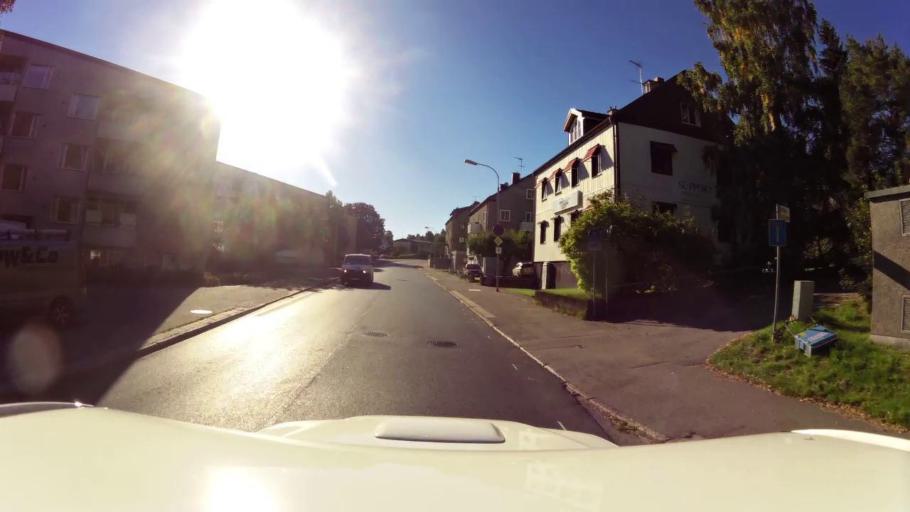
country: SE
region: OEstergoetland
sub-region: Linkopings Kommun
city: Linkoping
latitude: 58.3971
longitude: 15.6514
